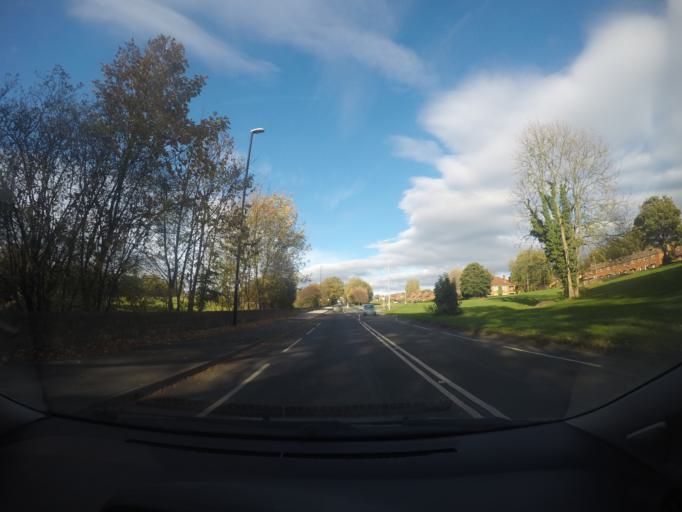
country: GB
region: England
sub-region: City and Borough of Leeds
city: Shadwell
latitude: 53.8315
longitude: -1.4756
